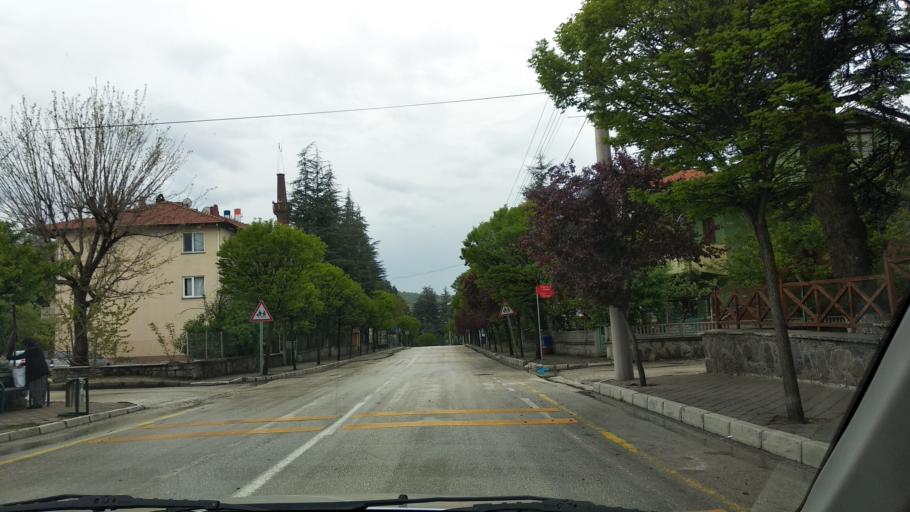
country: TR
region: Bolu
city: Seben
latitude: 40.4126
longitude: 31.5741
